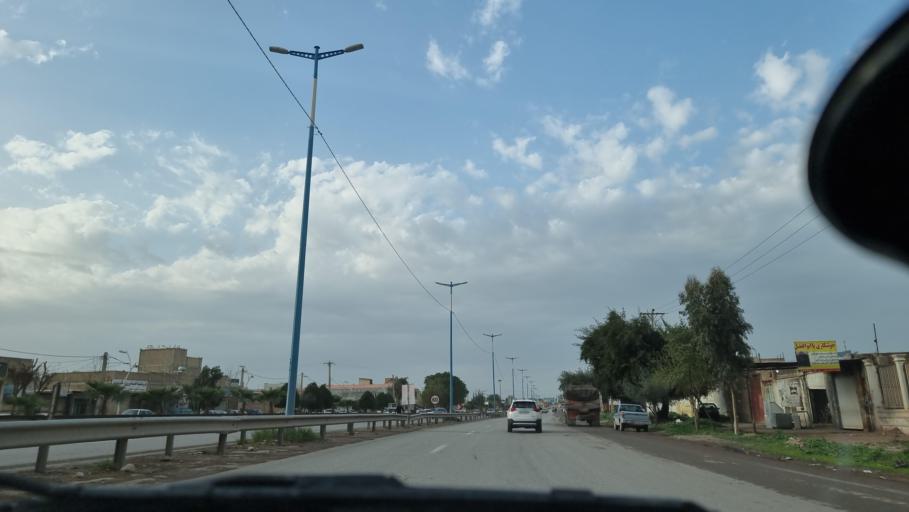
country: IR
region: Khuzestan
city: Boneh-ye Hoseyn Kaluli
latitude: 32.3013
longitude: 48.4287
